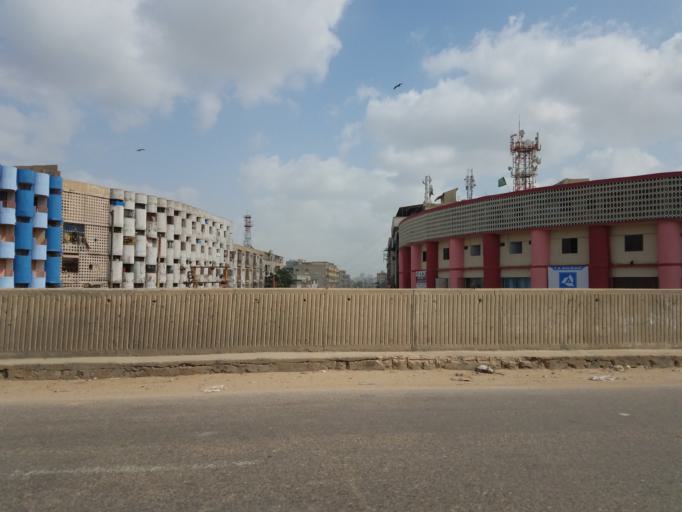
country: PK
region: Sindh
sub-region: Karachi District
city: Karachi
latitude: 24.9184
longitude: 67.0535
